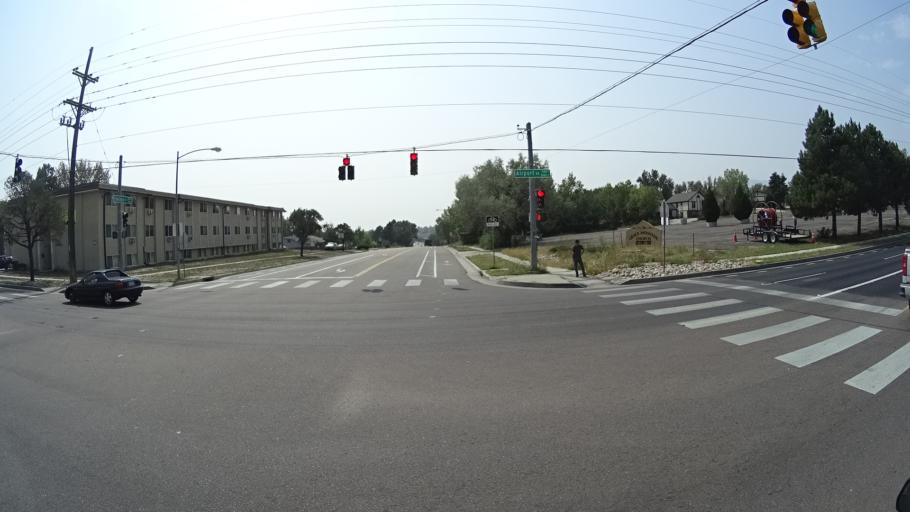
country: US
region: Colorado
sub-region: El Paso County
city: Stratmoor
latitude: 38.8254
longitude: -104.7681
